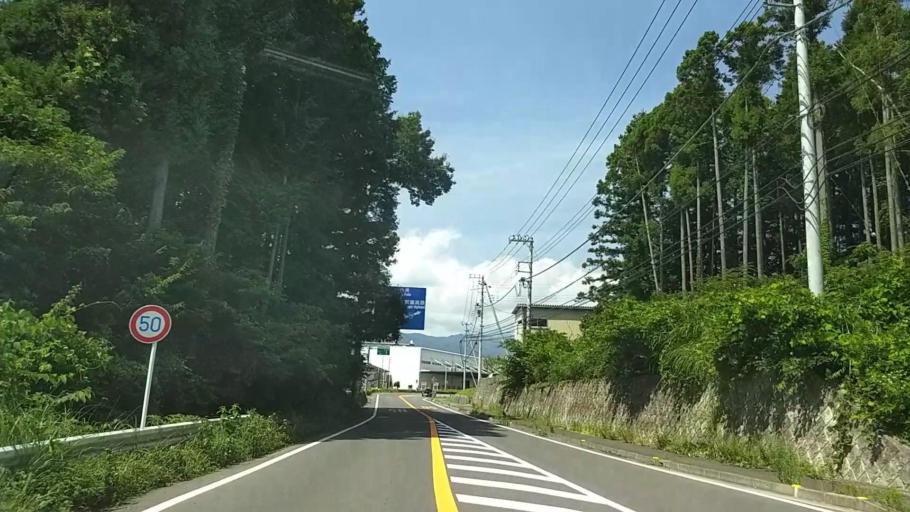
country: JP
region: Shizuoka
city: Fujinomiya
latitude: 35.3092
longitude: 138.6055
